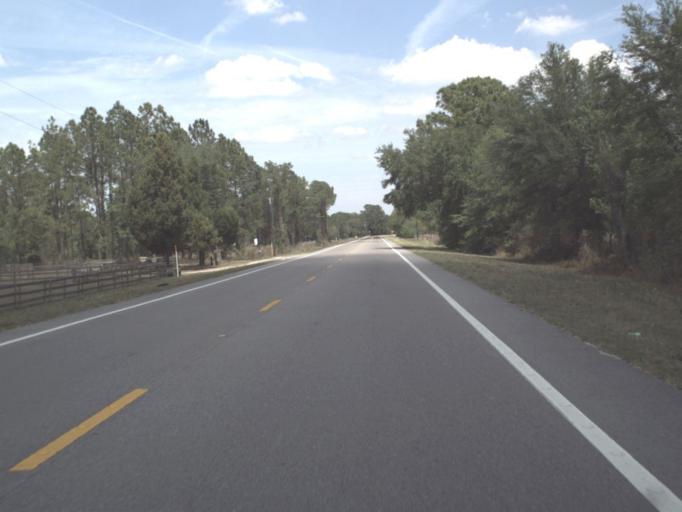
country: US
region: Florida
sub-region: Hernando County
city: Ridge Manor
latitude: 28.5423
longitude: -82.0909
